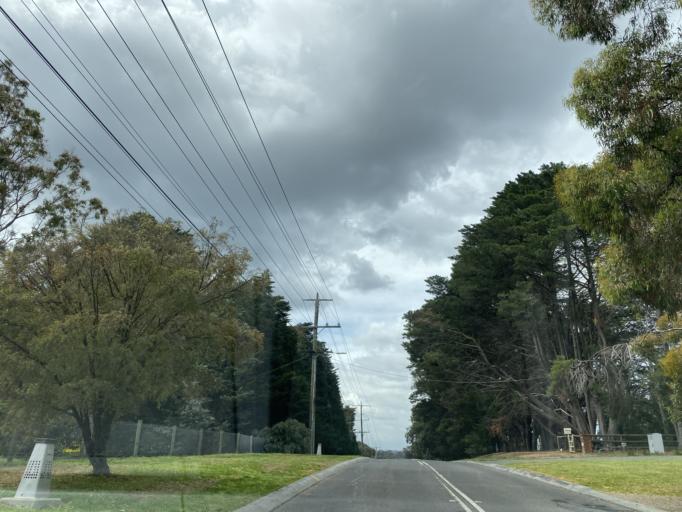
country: AU
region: Victoria
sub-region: Banyule
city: Lower Plenty
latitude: -37.7366
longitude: 145.1222
